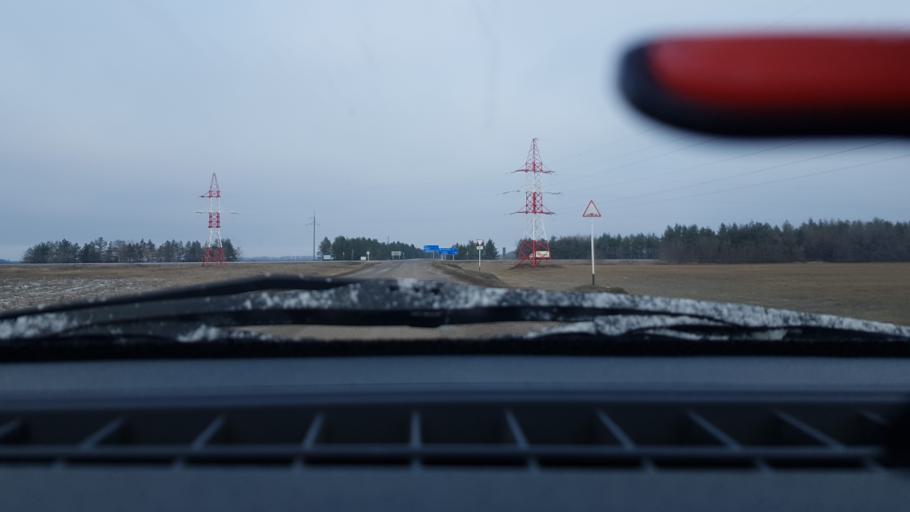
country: RU
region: Tatarstan
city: Kuybyshevskiy Zaton
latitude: 54.9441
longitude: 49.4521
